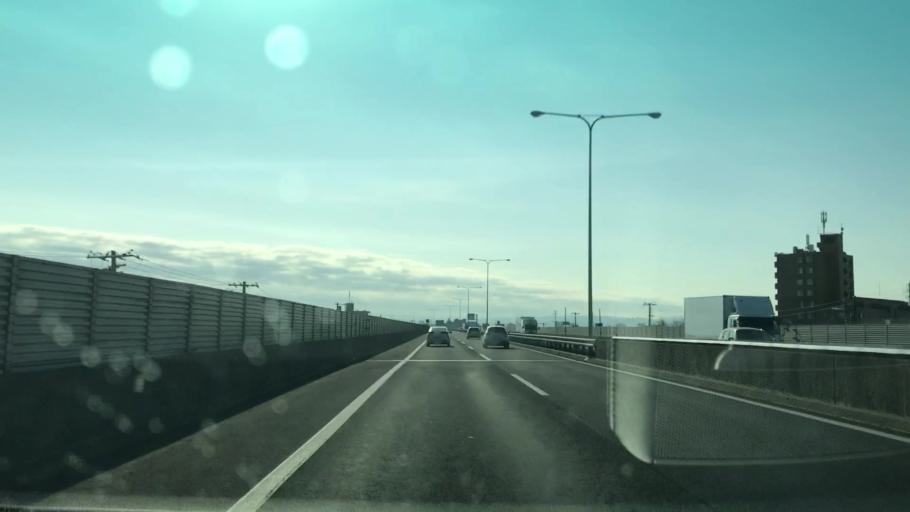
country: JP
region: Hokkaido
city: Sapporo
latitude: 43.0647
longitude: 141.4236
